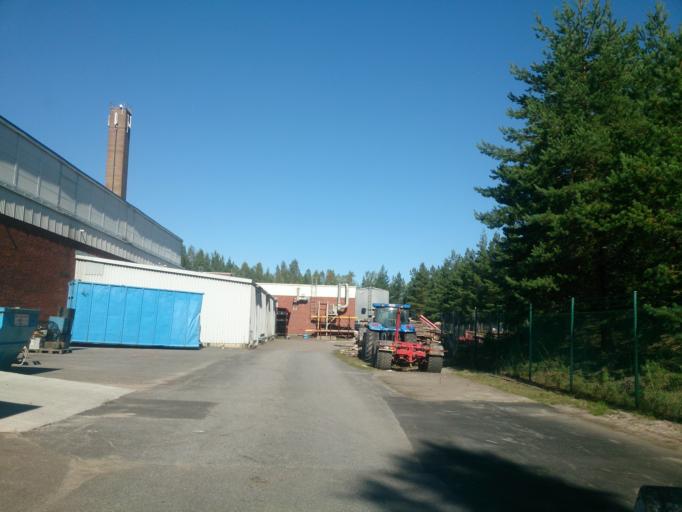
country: SE
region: OEstergoetland
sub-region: Atvidabergs Kommun
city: Atvidaberg
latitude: 58.2283
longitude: 15.9758
